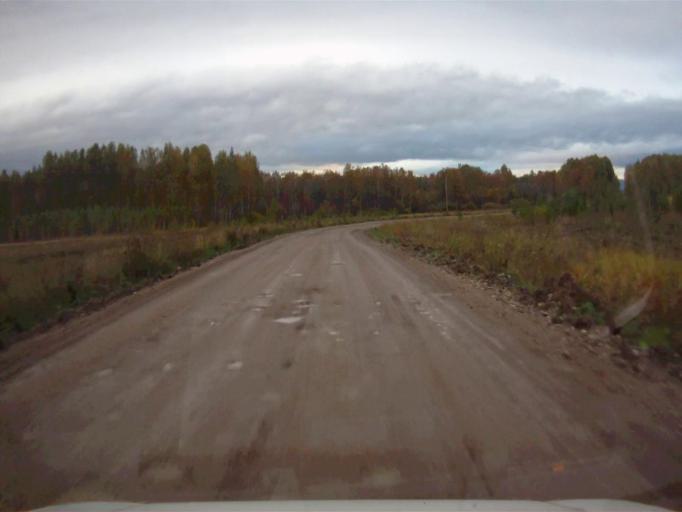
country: RU
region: Sverdlovsk
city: Mikhaylovsk
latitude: 56.1899
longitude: 59.1885
